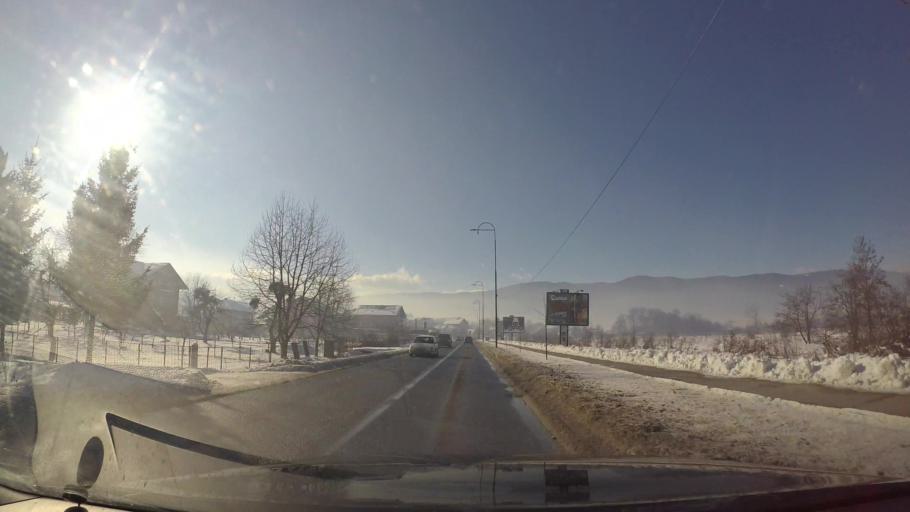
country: BA
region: Federation of Bosnia and Herzegovina
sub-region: Kanton Sarajevo
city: Sarajevo
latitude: 43.8138
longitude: 18.3519
